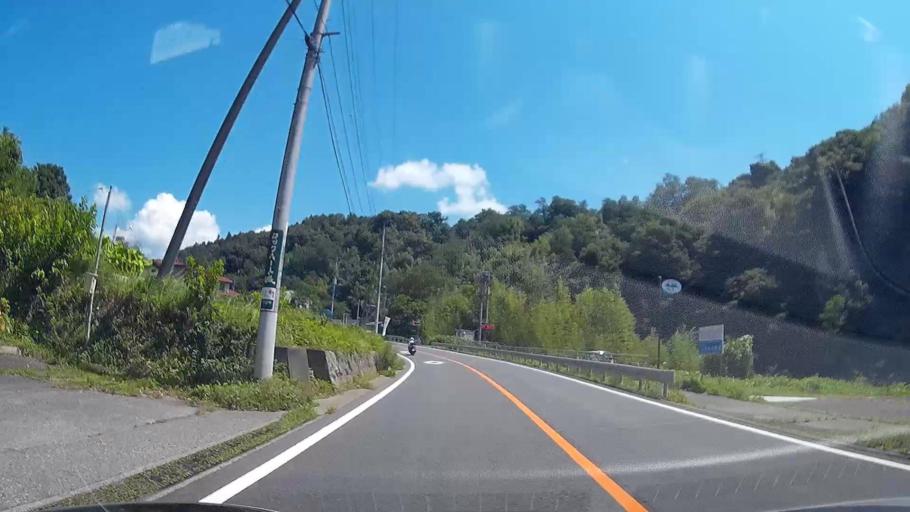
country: JP
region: Gunma
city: Numata
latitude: 36.6278
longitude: 139.0377
